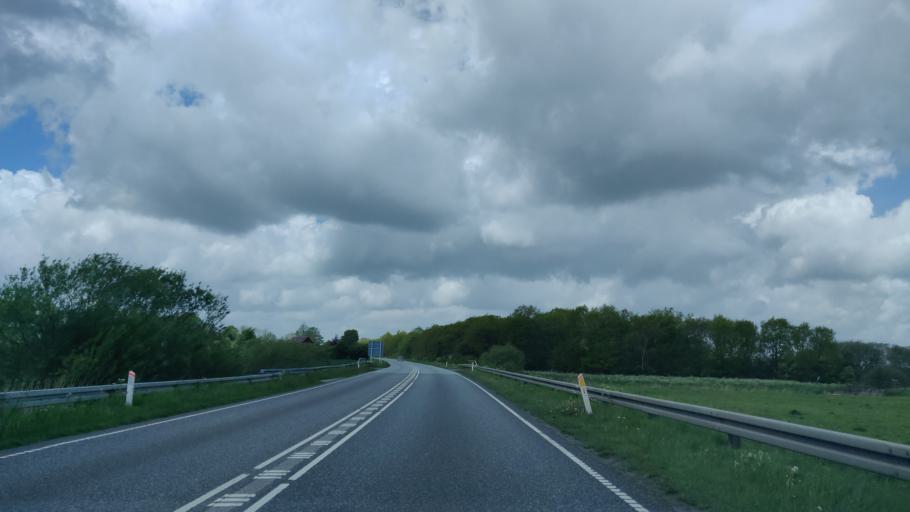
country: DK
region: Central Jutland
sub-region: Hedensted Kommune
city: Torring
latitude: 55.8392
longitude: 9.5068
